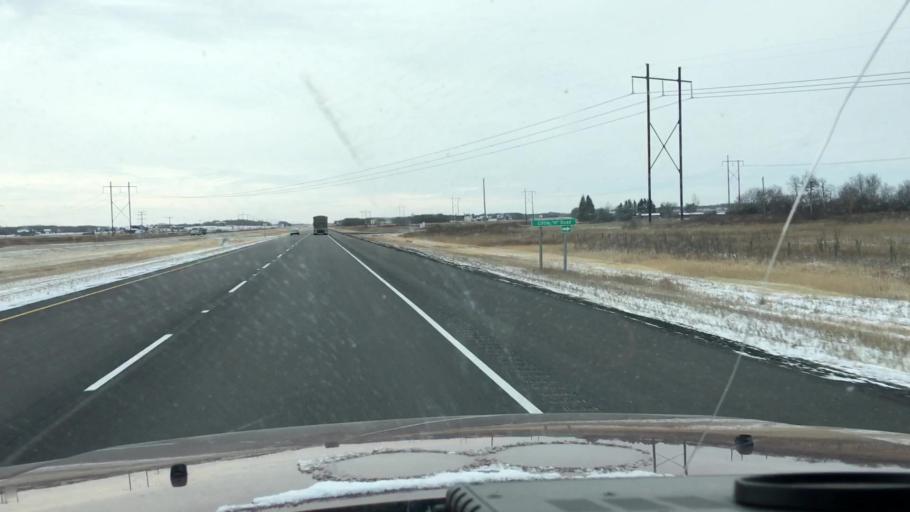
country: CA
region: Saskatchewan
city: Saskatoon
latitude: 51.9566
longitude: -106.5478
